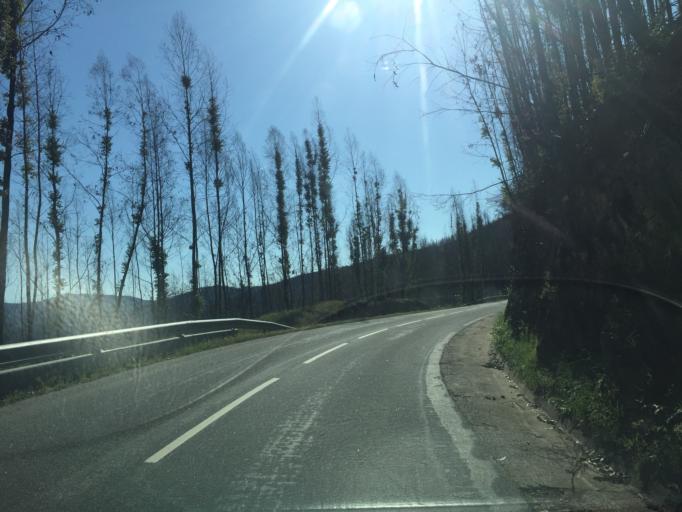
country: PT
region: Coimbra
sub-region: Pampilhosa da Serra
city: Pampilhosa da Serra
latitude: 40.0397
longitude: -7.9212
